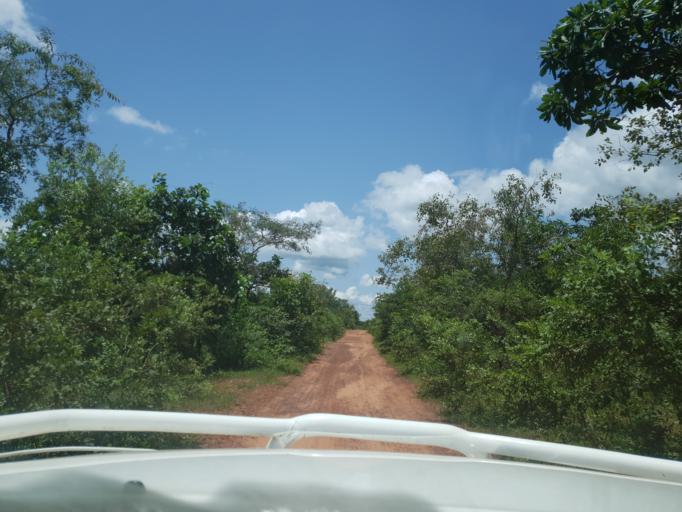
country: ML
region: Sikasso
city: Kadiolo
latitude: 10.7836
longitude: -5.7260
